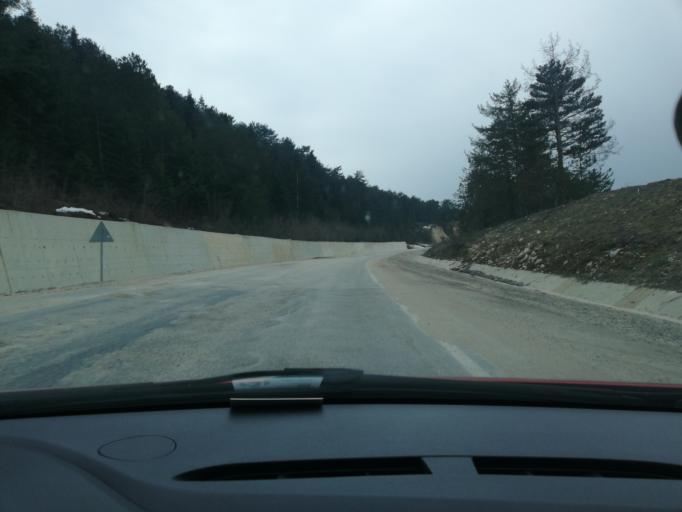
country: TR
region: Kastamonu
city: Pinarbasi
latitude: 41.5610
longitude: 33.0870
